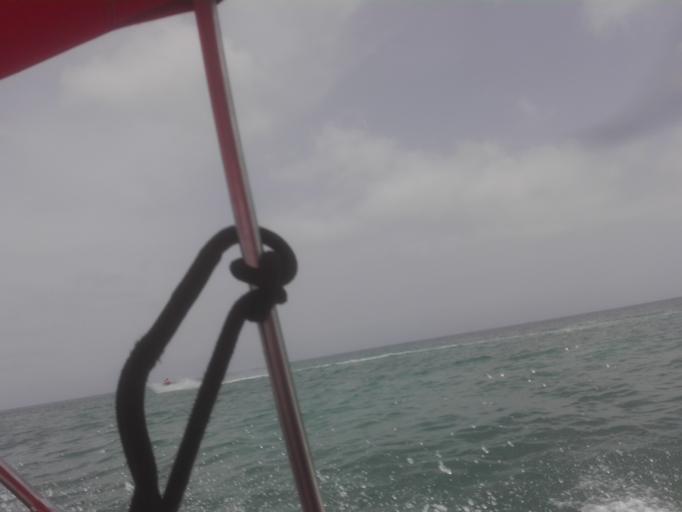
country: CO
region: Bolivar
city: Turbana
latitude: 10.2216
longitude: -75.6110
